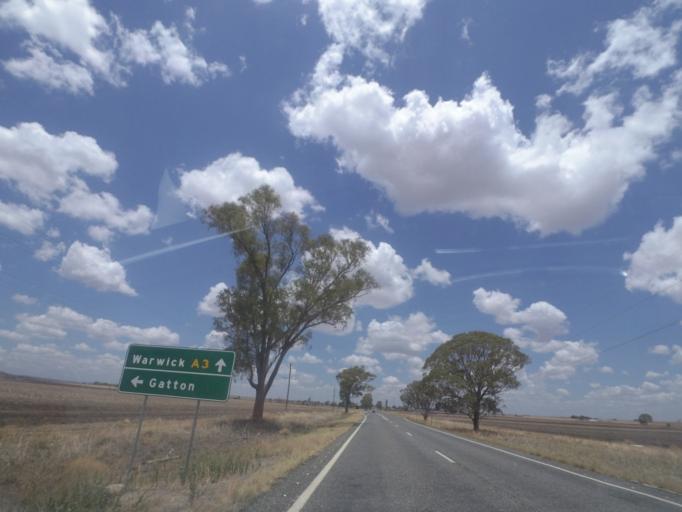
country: AU
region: Queensland
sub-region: Toowoomba
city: Top Camp
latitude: -27.9200
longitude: 151.9825
